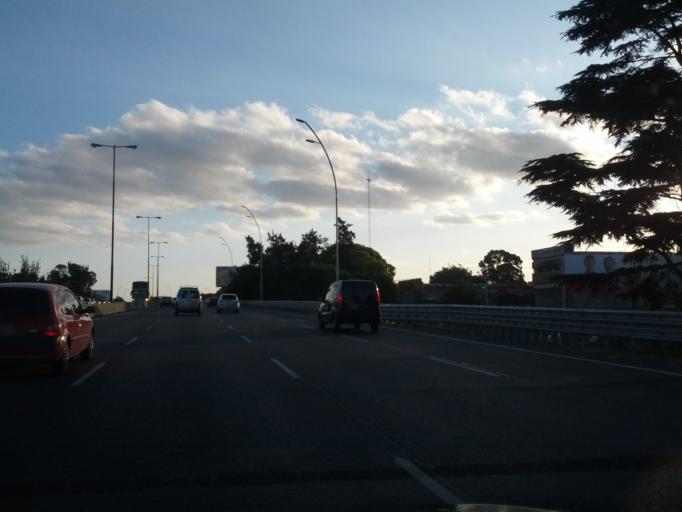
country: AR
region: Buenos Aires
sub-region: Partido de General San Martin
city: General San Martin
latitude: -34.5945
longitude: -58.5211
